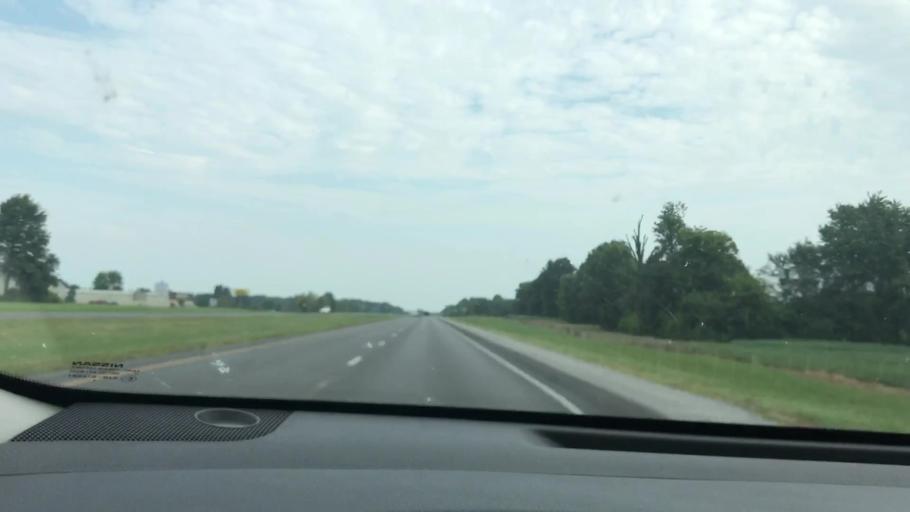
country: US
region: Kentucky
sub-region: Calloway County
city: Murray
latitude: 36.6895
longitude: -88.3029
